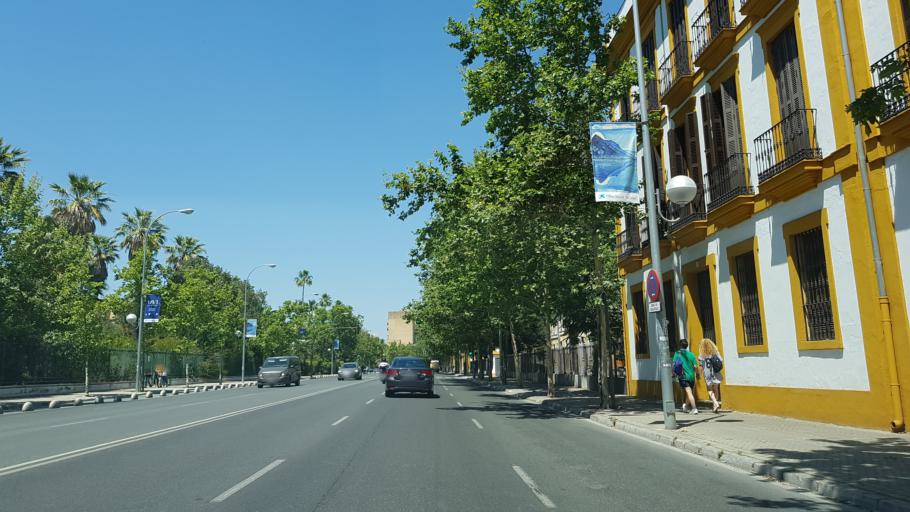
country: ES
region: Andalusia
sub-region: Provincia de Sevilla
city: Sevilla
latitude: 37.3746
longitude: -5.9851
